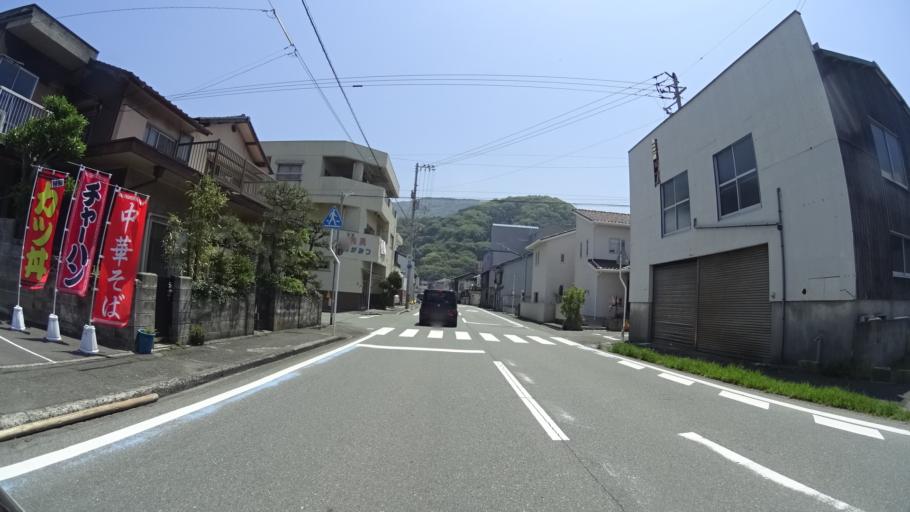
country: JP
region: Ehime
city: Ozu
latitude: 33.6159
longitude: 132.4812
